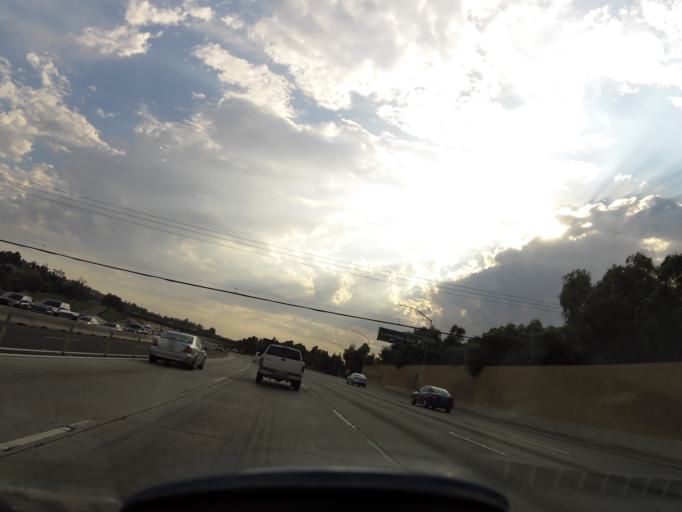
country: US
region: California
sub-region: Orange County
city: Yorba Linda
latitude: 33.8534
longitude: -117.8113
